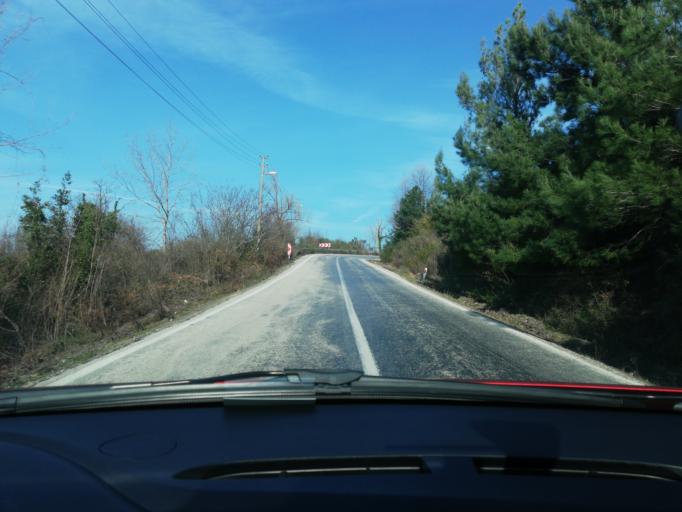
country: TR
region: Bartin
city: Kurucasile
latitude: 41.8463
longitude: 32.7406
